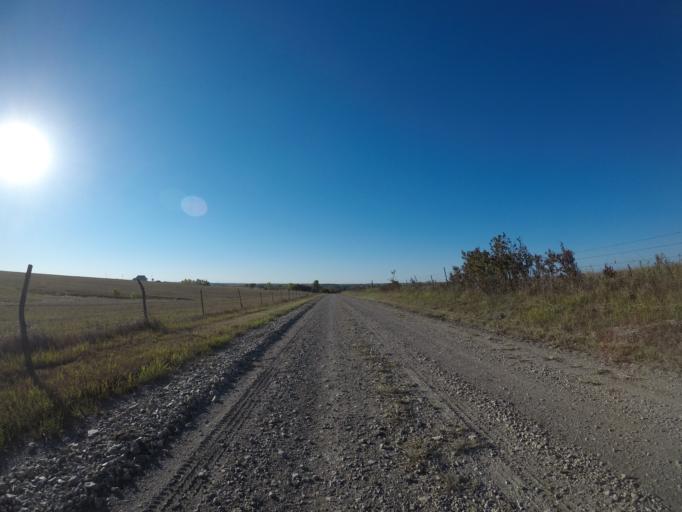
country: US
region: Kansas
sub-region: Wabaunsee County
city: Alma
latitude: 38.9312
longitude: -96.4641
